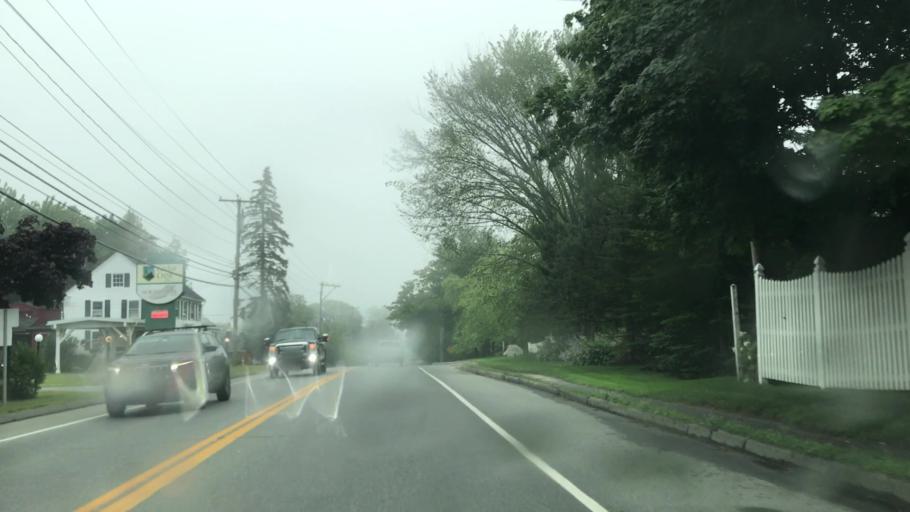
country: US
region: Maine
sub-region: Knox County
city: Camden
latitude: 44.2019
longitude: -69.0756
